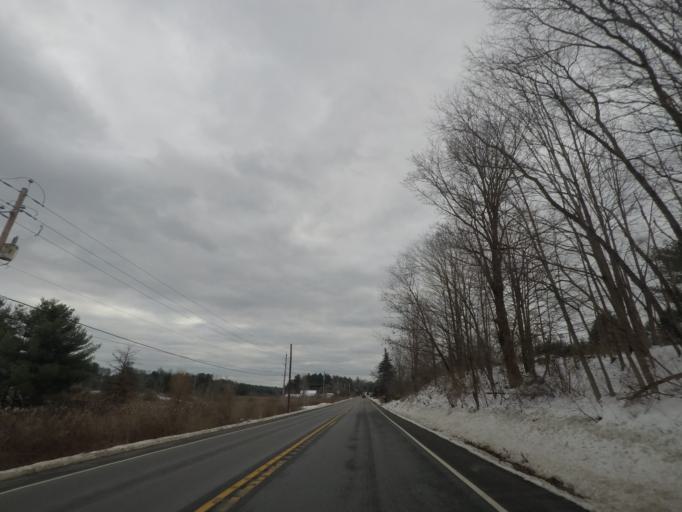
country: US
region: New York
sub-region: Rensselaer County
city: West Sand Lake
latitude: 42.6241
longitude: -73.6035
